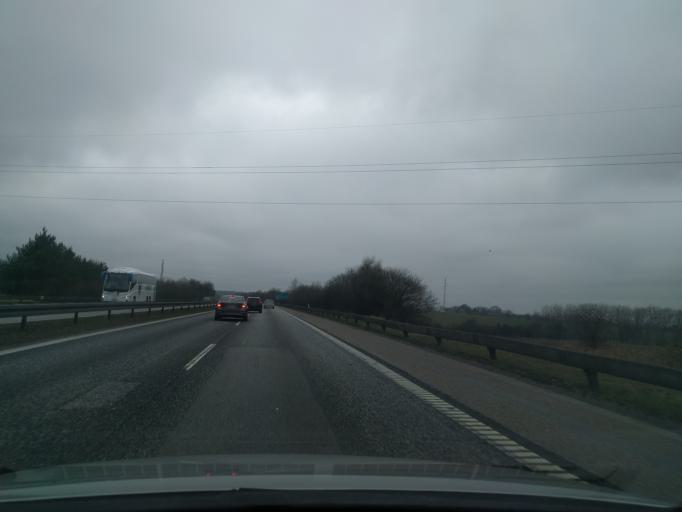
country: DK
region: Zealand
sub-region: Soro Kommune
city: Soro
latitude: 55.4523
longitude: 11.5424
